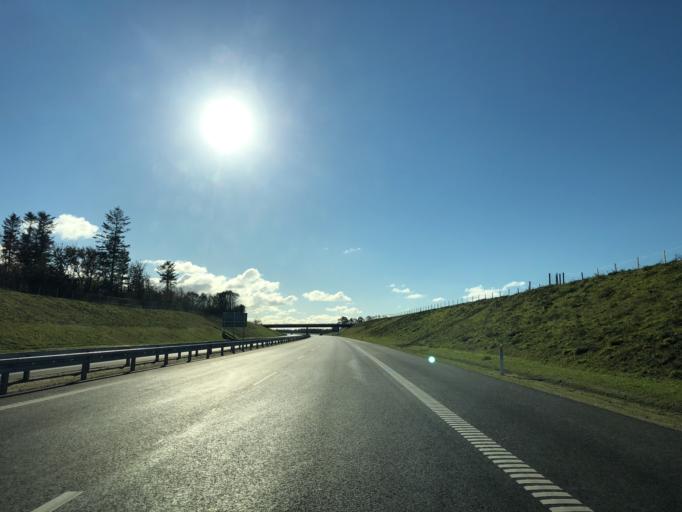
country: DK
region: Central Jutland
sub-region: Herning Kommune
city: Avlum
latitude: 56.3080
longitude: 8.7268
